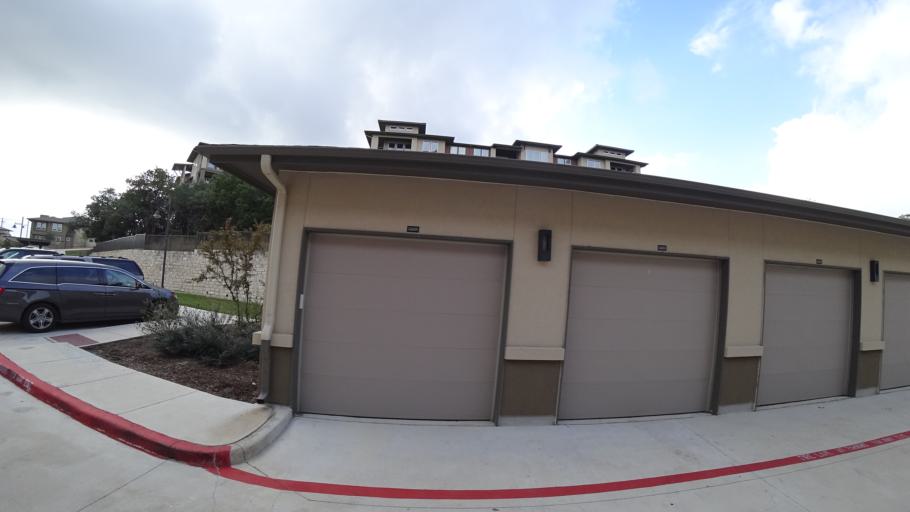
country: US
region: Texas
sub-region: Travis County
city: Hudson Bend
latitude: 30.3843
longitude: -97.8735
